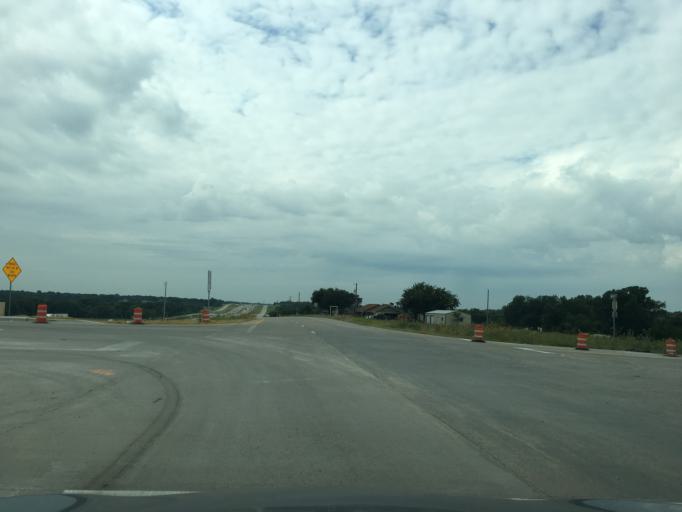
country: US
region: Texas
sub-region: Collin County
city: Melissa
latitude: 33.3098
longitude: -96.5917
